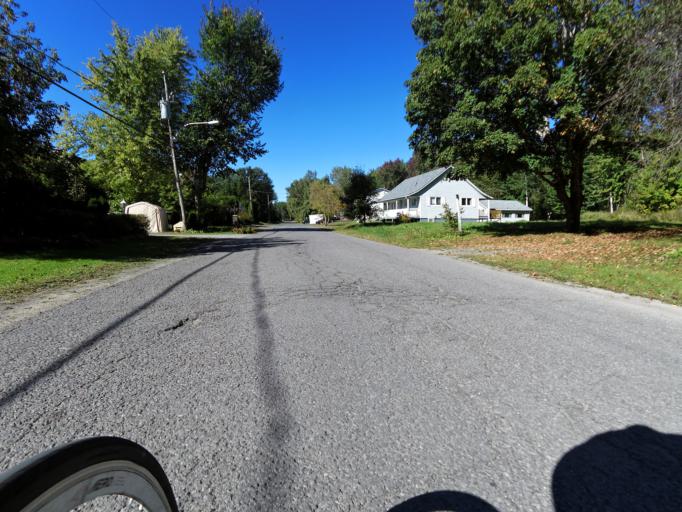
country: CA
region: Quebec
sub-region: Outaouais
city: Gatineau
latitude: 45.4760
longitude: -75.6123
